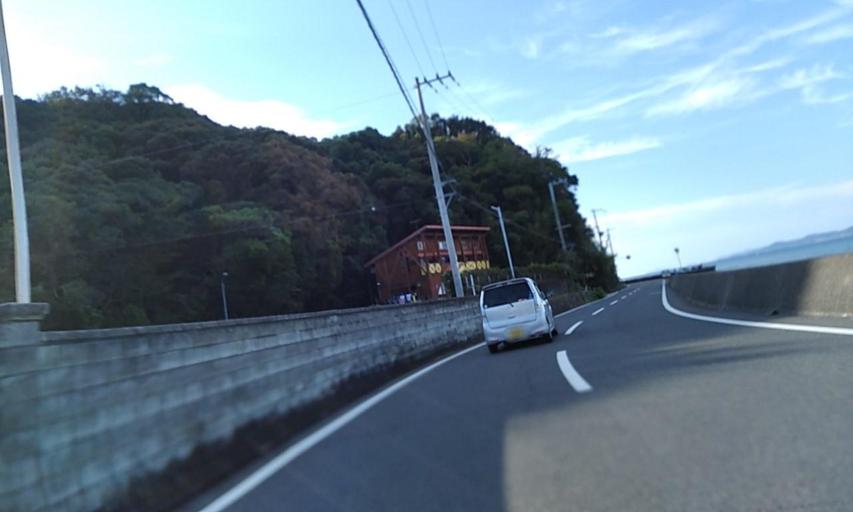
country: JP
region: Wakayama
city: Tanabe
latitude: 33.6934
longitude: 135.3461
